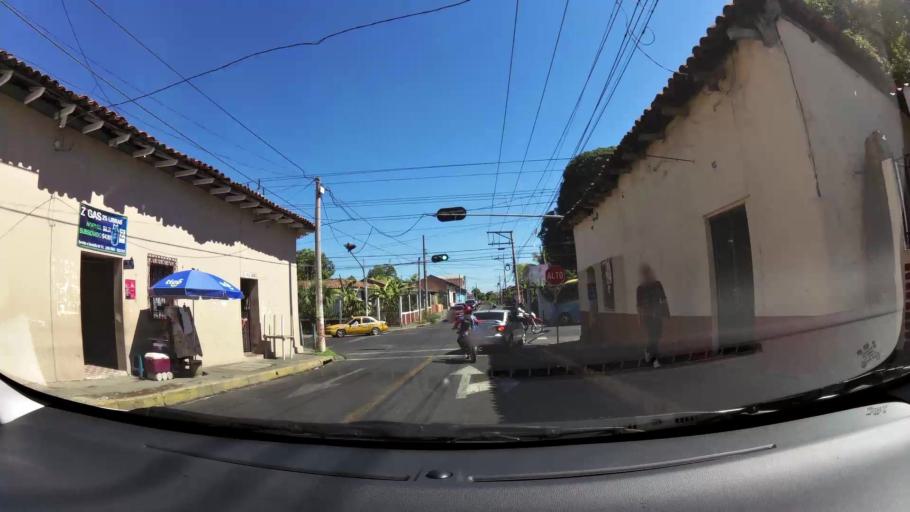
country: SV
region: San Miguel
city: San Miguel
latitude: 13.4782
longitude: -88.1721
